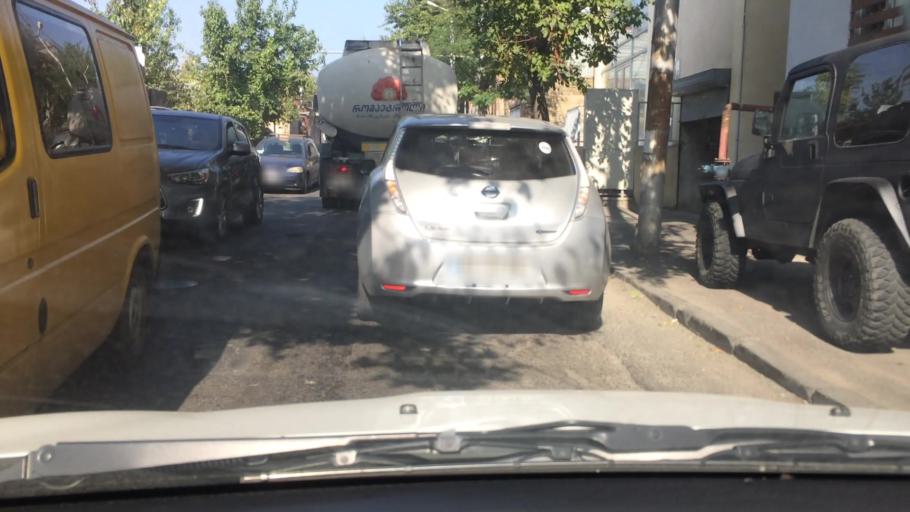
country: GE
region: T'bilisi
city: Tbilisi
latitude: 41.6913
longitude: 44.8247
